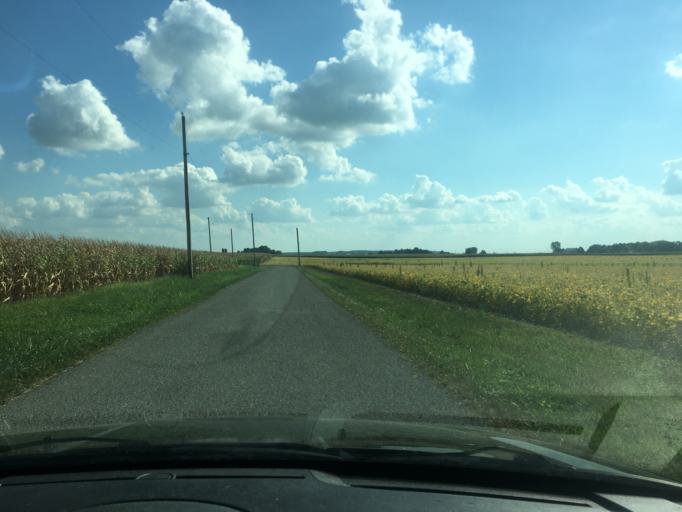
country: US
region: Ohio
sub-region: Logan County
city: West Liberty
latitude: 40.2469
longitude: -83.7458
